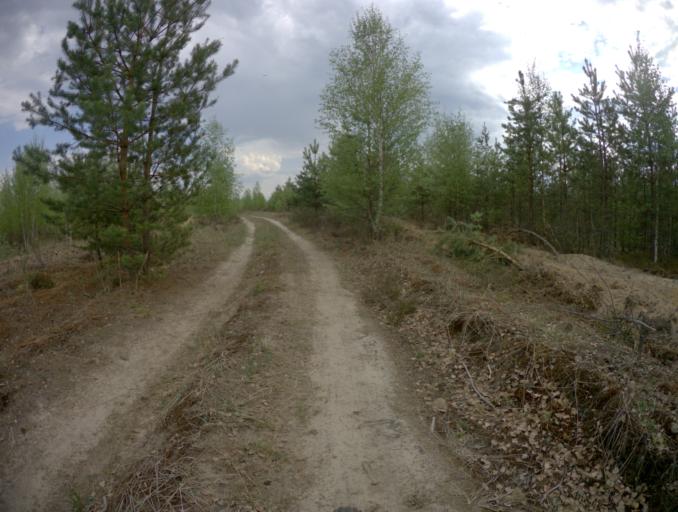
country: RU
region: Ivanovo
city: Talitsy
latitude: 56.4483
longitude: 42.2290
